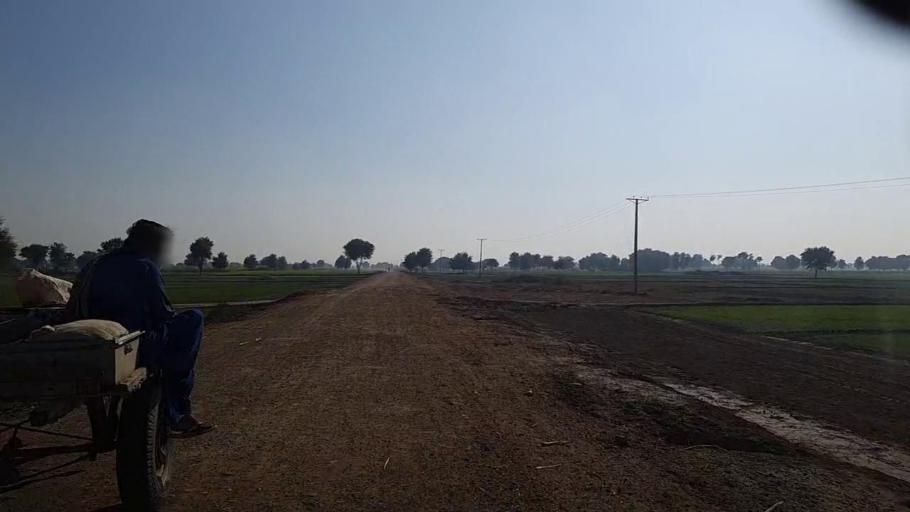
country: PK
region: Sindh
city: Darya Khan Marri
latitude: 26.6649
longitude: 68.3363
